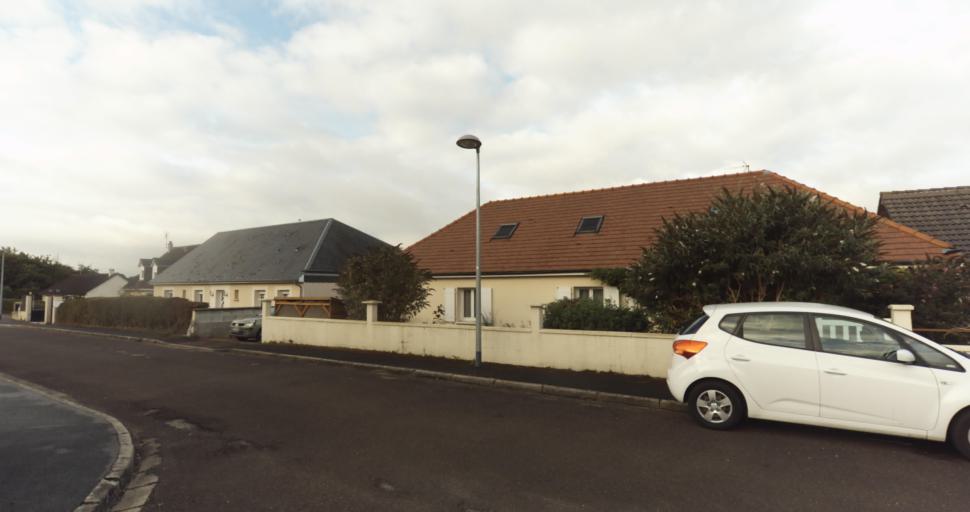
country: FR
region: Lower Normandy
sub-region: Departement de l'Orne
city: Vimoutiers
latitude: 48.9230
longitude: 0.2073
